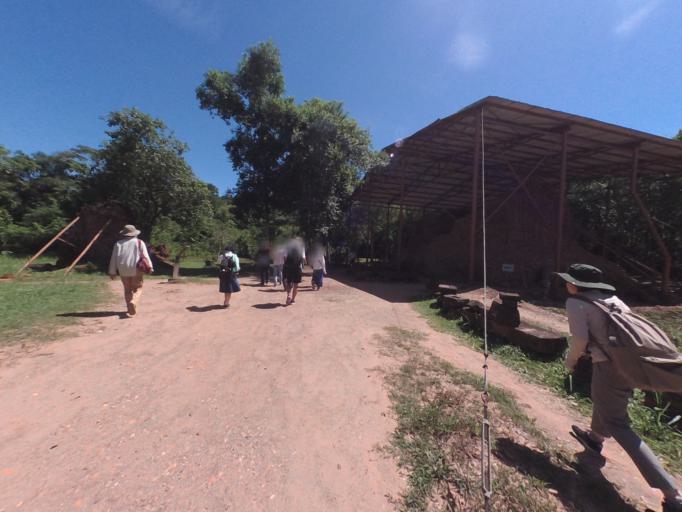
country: VN
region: Quang Nam
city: Dai Loc
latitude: 15.7648
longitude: 108.1251
